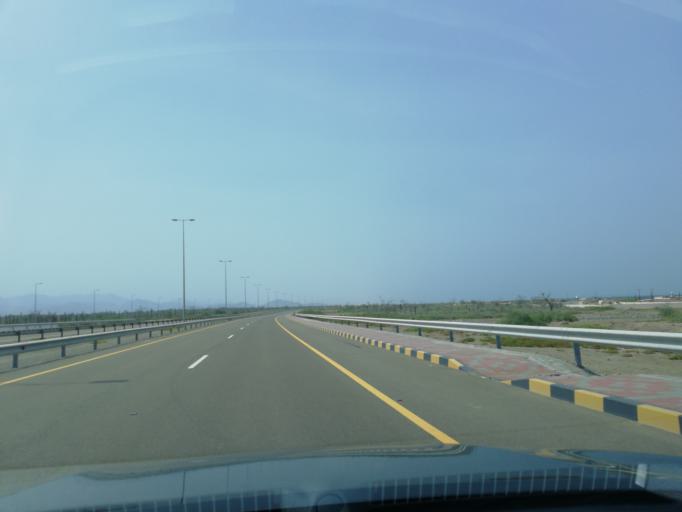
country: OM
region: Al Batinah
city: Shinas
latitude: 24.8712
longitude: 56.4080
